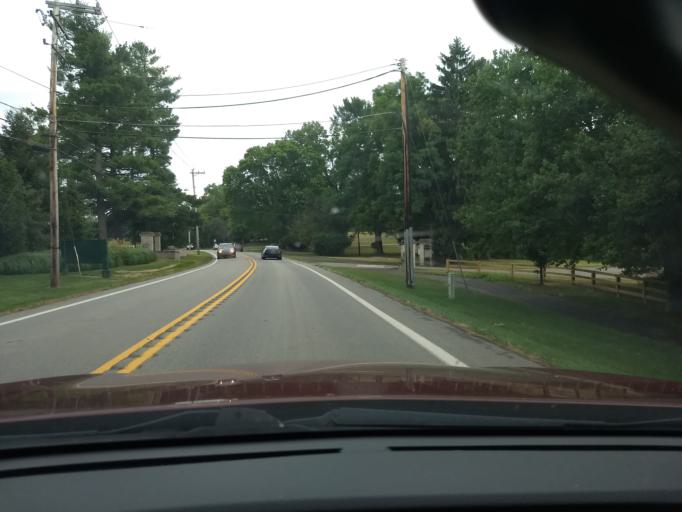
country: US
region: Pennsylvania
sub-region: Butler County
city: Mars
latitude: 40.6651
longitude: -80.0181
